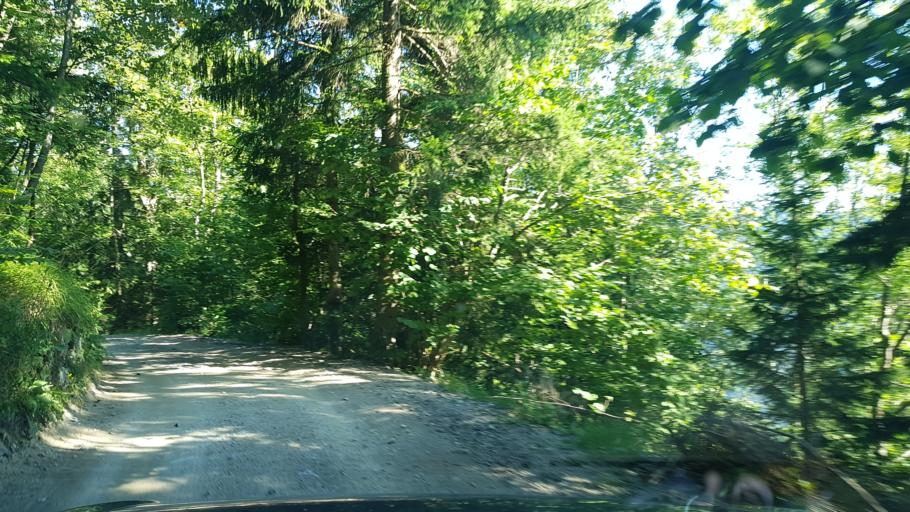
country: SI
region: Ravne na Koroskem
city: Kotlje
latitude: 46.4837
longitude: 14.9351
